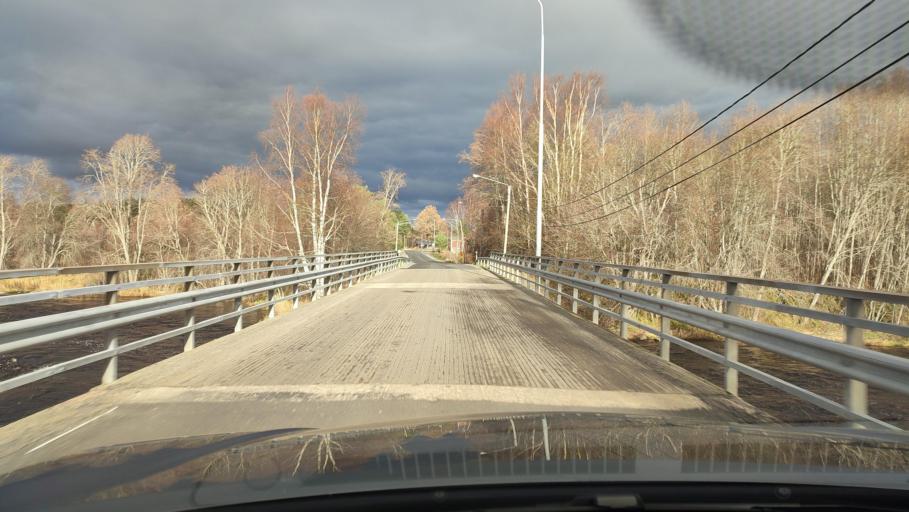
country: FI
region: Southern Ostrobothnia
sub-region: Suupohja
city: Karijoki
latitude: 62.2386
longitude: 21.5774
